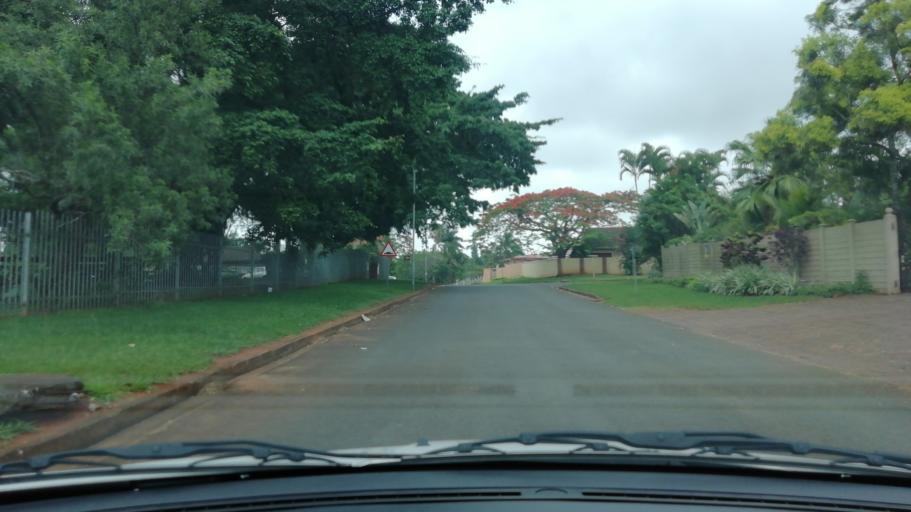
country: ZA
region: KwaZulu-Natal
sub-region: uThungulu District Municipality
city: Empangeni
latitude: -28.7669
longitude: 31.8971
